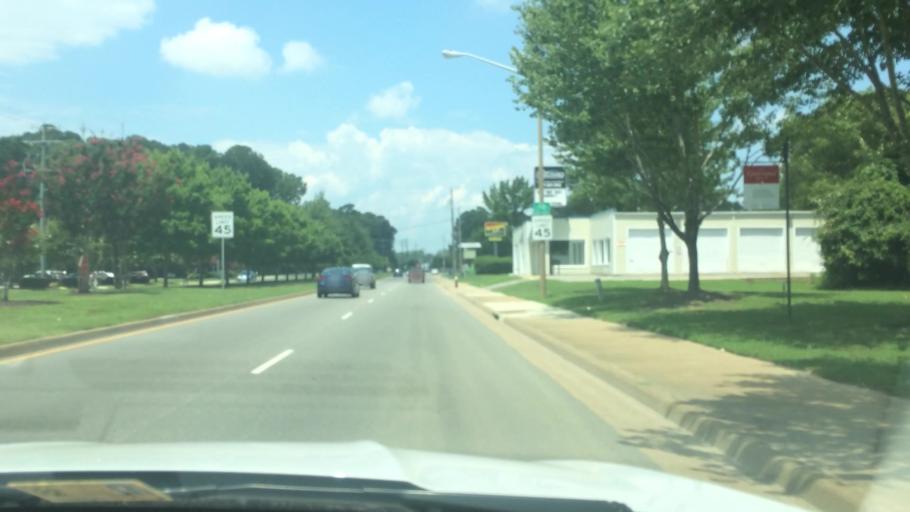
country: US
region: Virginia
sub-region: York County
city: Yorktown
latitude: 37.1517
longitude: -76.5538
